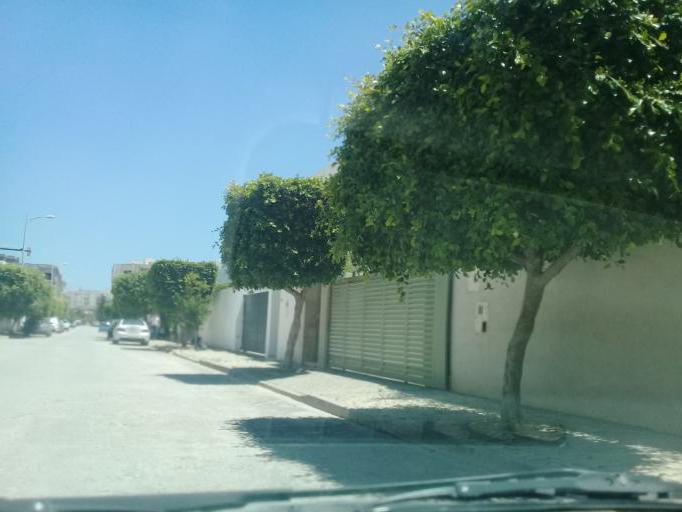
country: TN
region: Tunis
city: La Goulette
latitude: 36.8436
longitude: 10.2735
